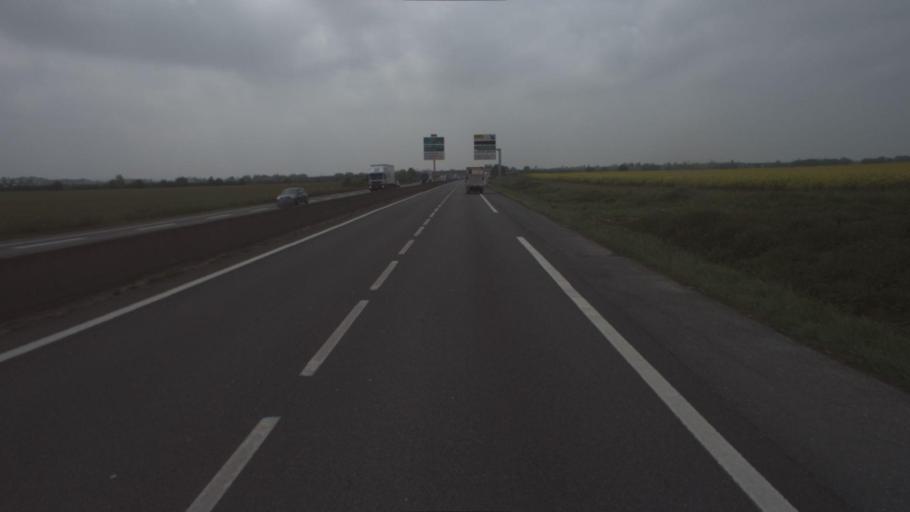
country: FR
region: Ile-de-France
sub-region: Departement de Seine-et-Marne
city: Mitry-Mory
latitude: 49.0059
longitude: 2.6458
